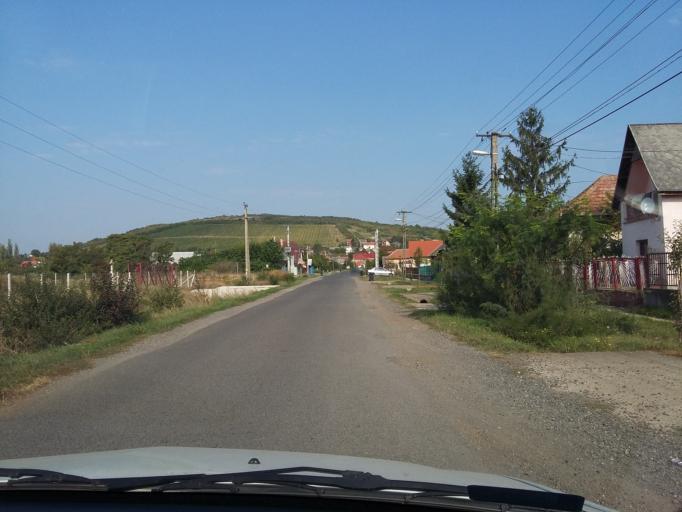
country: HU
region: Borsod-Abauj-Zemplen
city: Bekecs
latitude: 48.1478
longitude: 21.1795
